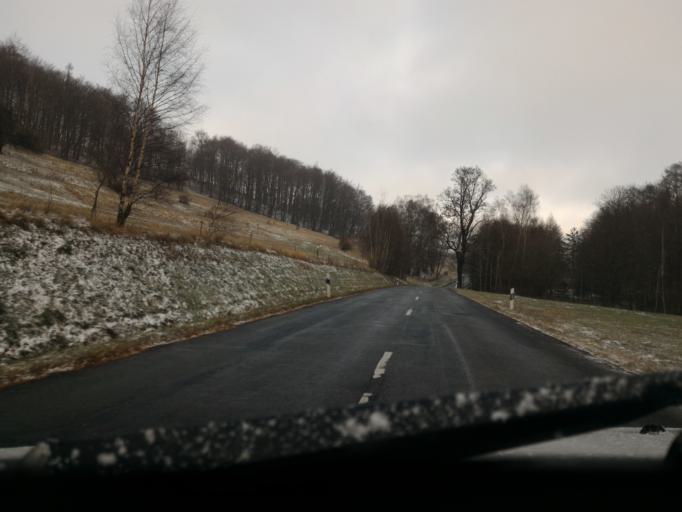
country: DE
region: Saxony
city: Grossschonau
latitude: 50.8625
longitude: 14.6596
